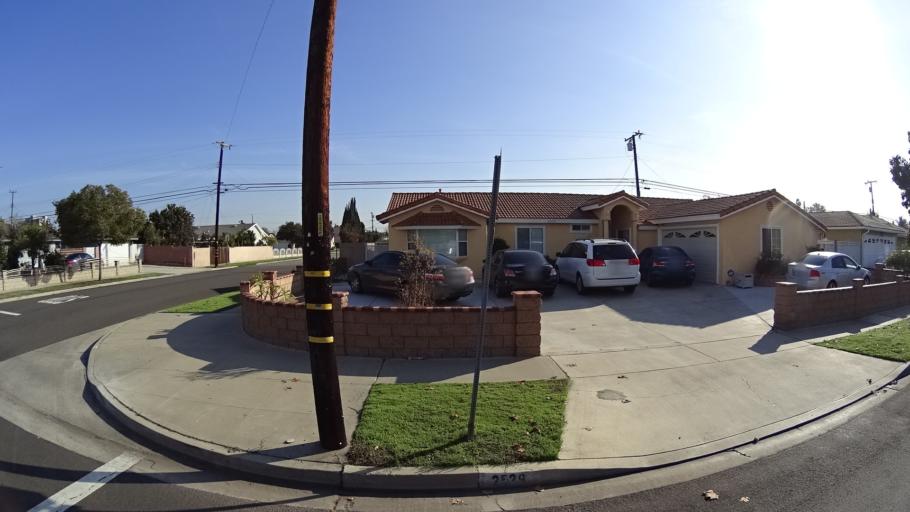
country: US
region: California
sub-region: Orange County
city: Santa Ana
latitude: 33.7711
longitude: -117.8991
